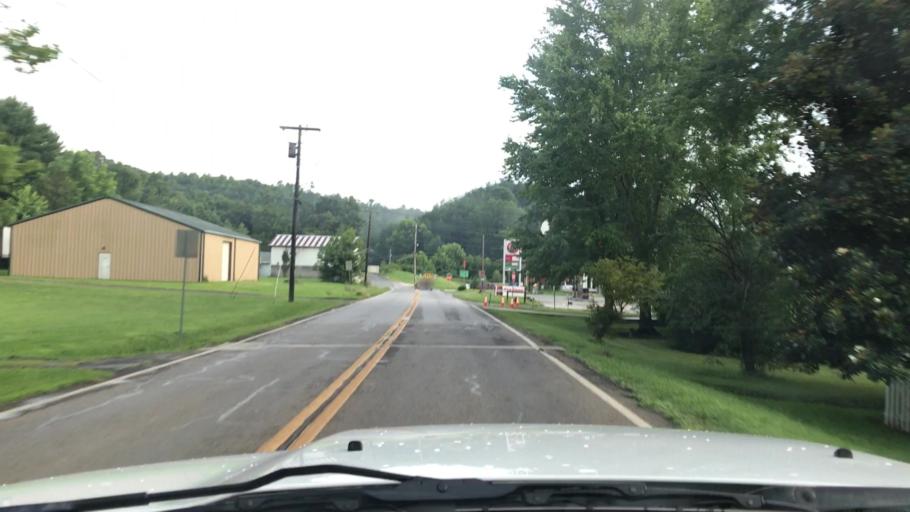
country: US
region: Georgia
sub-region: Fannin County
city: Blue Ridge
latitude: 34.9159
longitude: -84.2765
